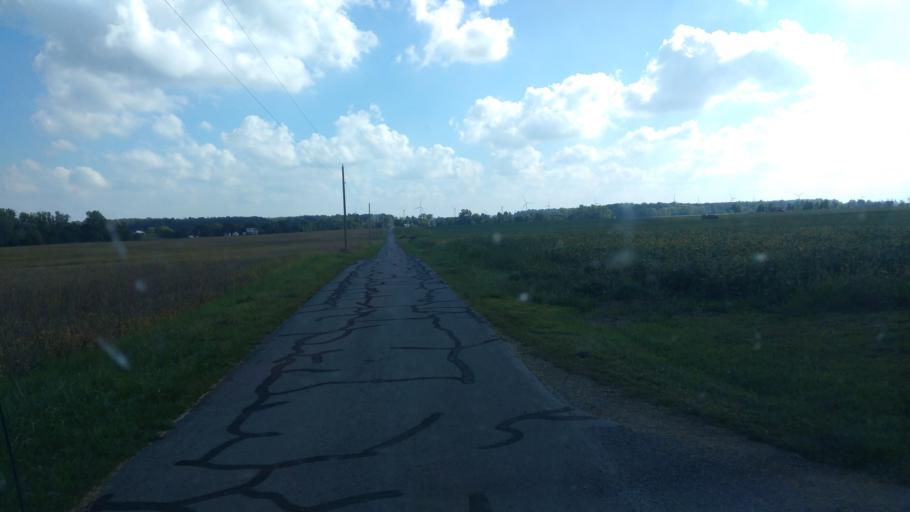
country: US
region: Ohio
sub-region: Hancock County
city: Arlington
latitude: 40.8405
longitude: -83.7085
